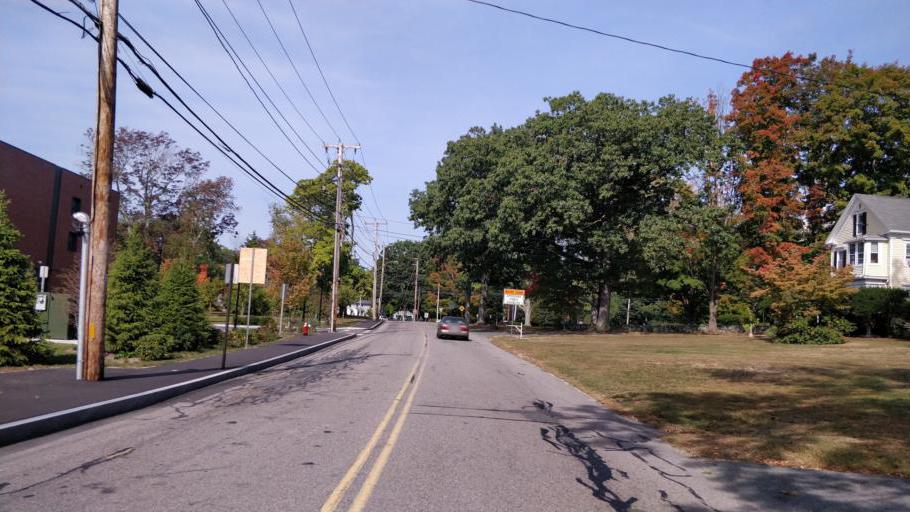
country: US
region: Massachusetts
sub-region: Bristol County
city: Norton Center
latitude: 41.9687
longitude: -71.1808
